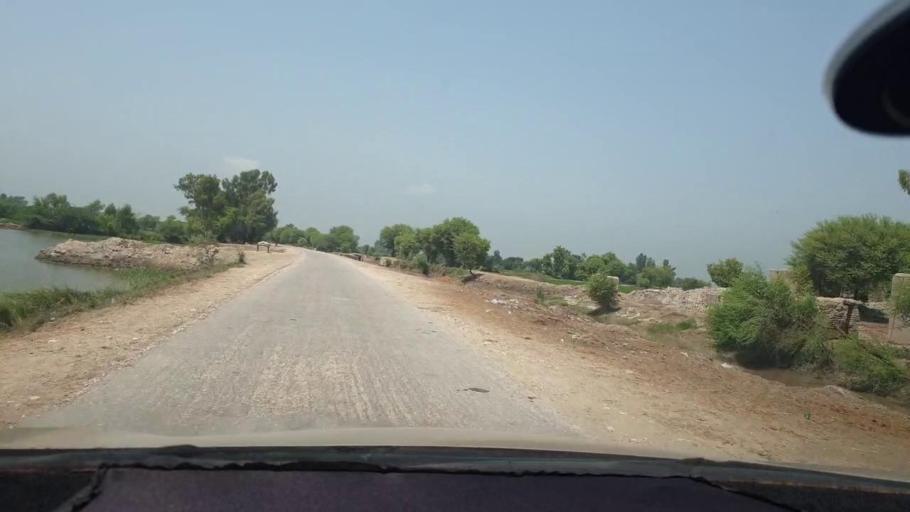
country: PK
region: Sindh
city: Kambar
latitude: 27.6581
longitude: 67.9565
